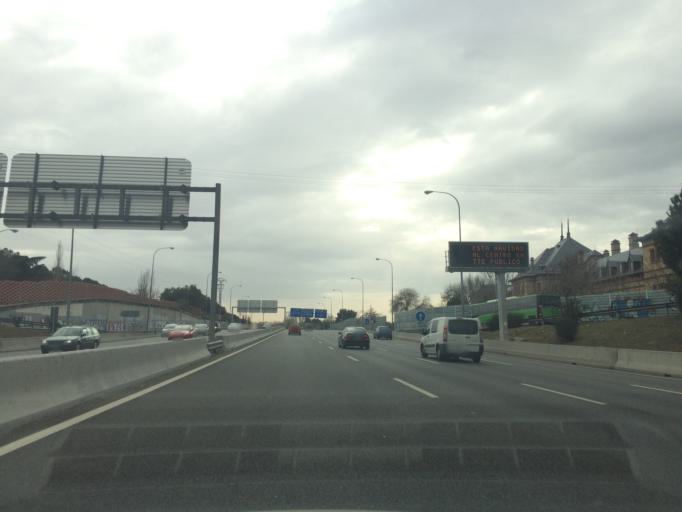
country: ES
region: Madrid
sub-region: Provincia de Madrid
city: Tetuan de las Victorias
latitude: 40.4686
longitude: -3.7500
